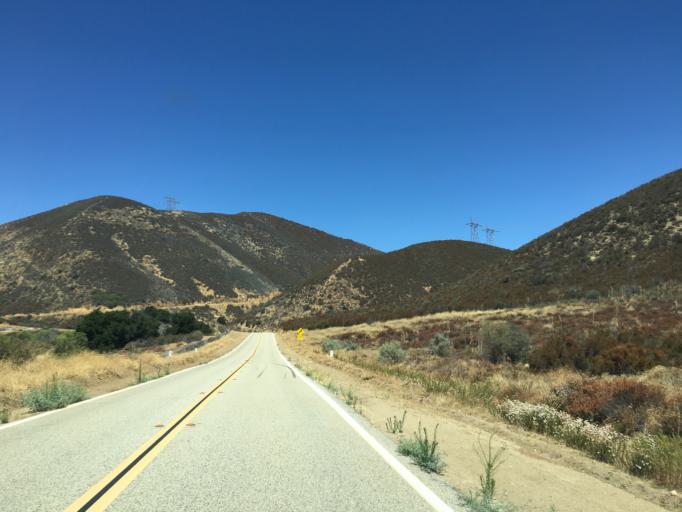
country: US
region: California
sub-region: Los Angeles County
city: Green Valley
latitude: 34.5896
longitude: -118.3774
